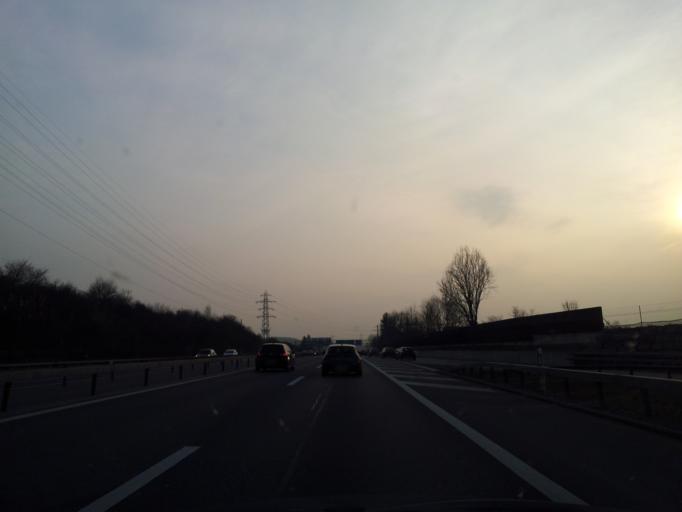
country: CH
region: Zug
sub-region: Zug
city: Cham
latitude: 47.1984
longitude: 8.4582
